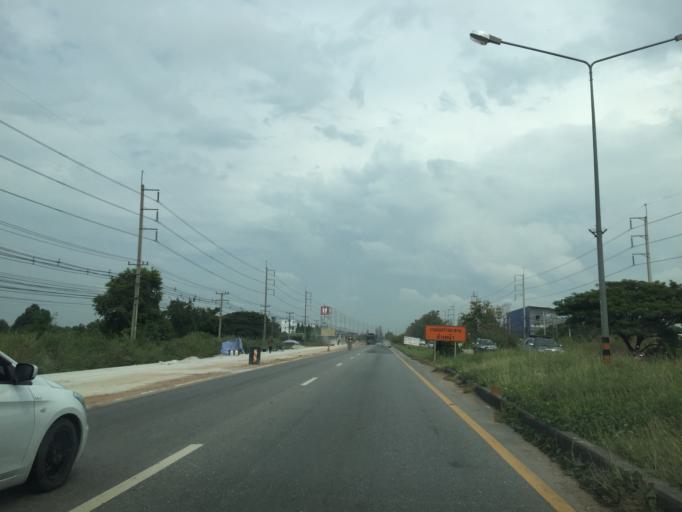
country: TH
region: Lamphun
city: Lamphun
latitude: 18.6021
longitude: 99.0432
